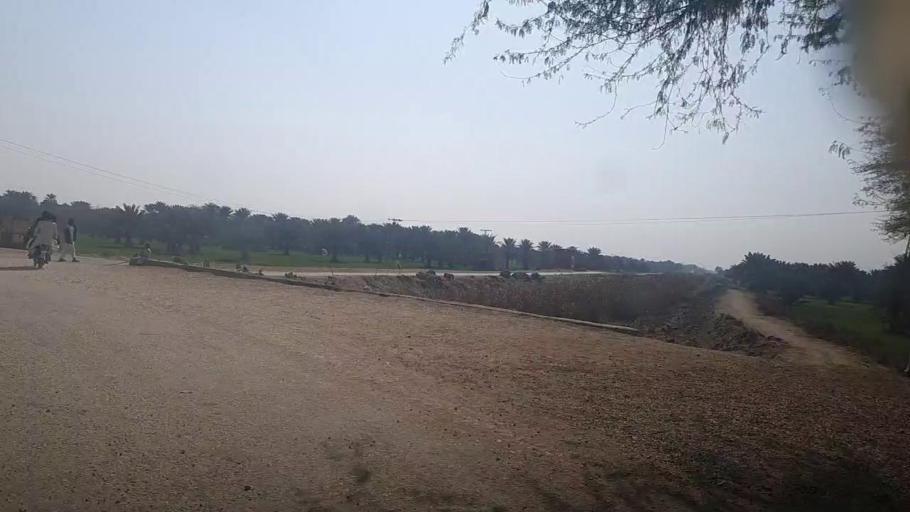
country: PK
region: Sindh
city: Khairpur
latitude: 27.4597
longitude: 68.8156
